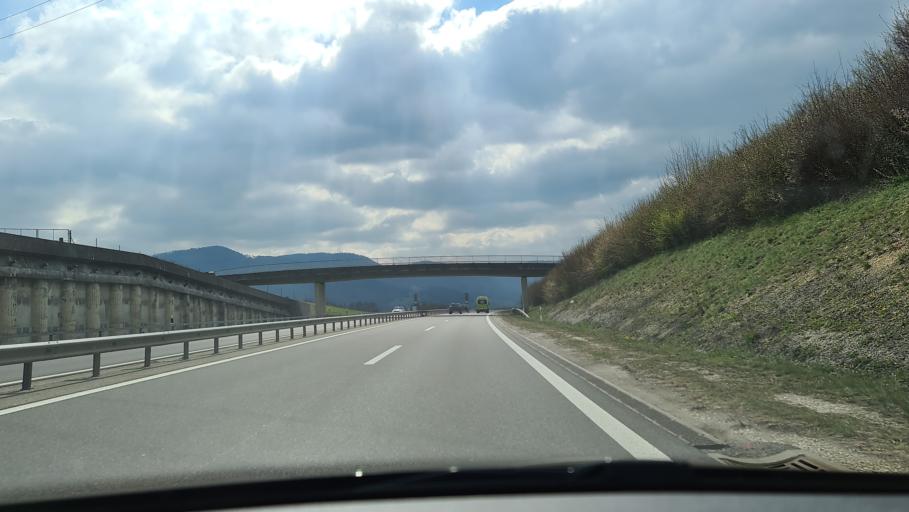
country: CH
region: Jura
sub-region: Delemont District
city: Courfaivre
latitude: 47.3470
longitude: 7.2845
